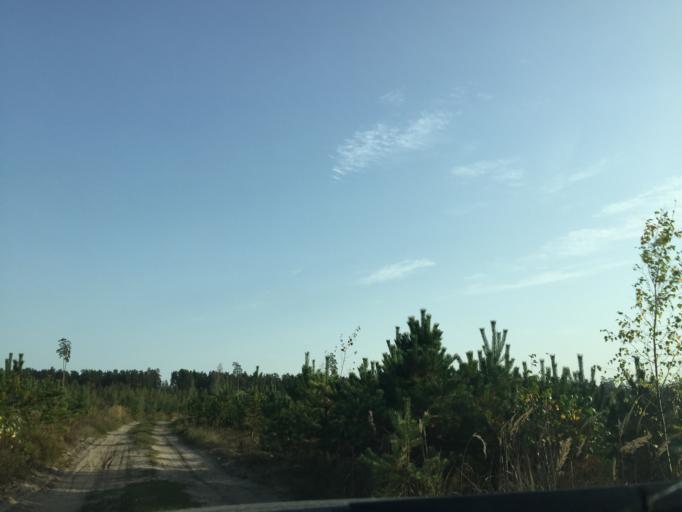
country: LV
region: Garkalne
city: Garkalne
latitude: 56.9692
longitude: 24.4194
